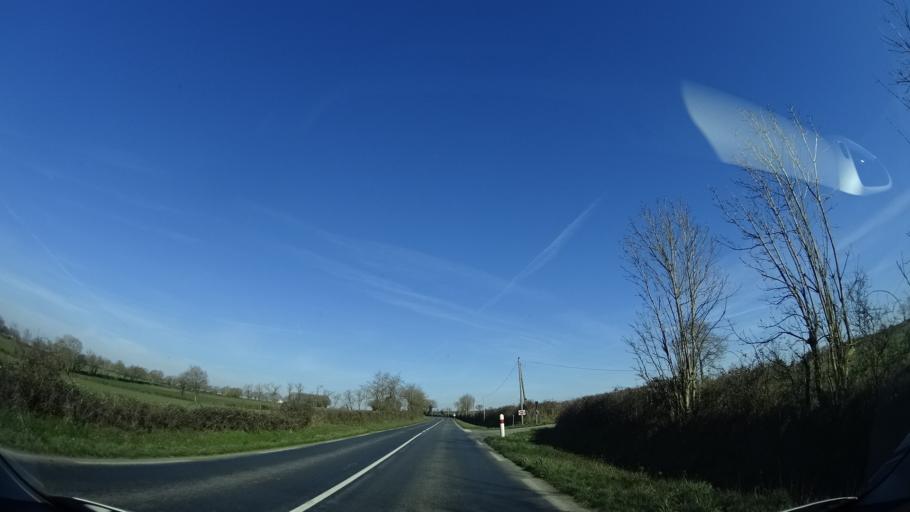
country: FR
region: Poitou-Charentes
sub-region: Departement des Deux-Sevres
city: Saint-Pierre-des-Echaubrognes
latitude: 46.9462
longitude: -0.7532
